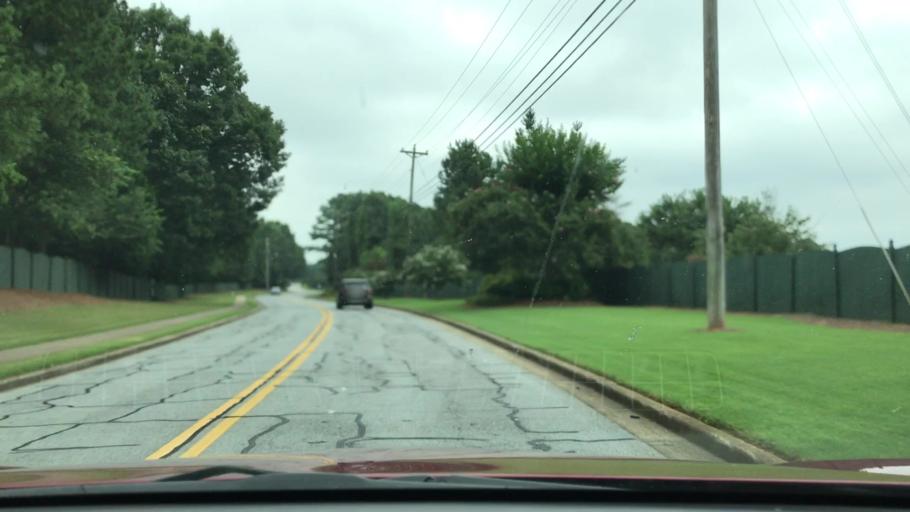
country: US
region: Georgia
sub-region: Gwinnett County
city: Suwanee
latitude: 34.0092
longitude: -84.0242
